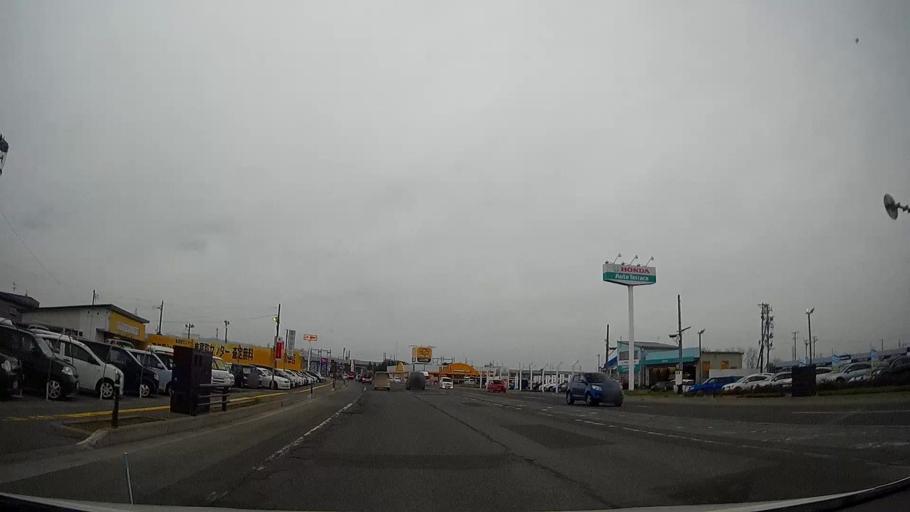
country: JP
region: Aomori
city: Aomori Shi
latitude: 40.8331
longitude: 140.6992
